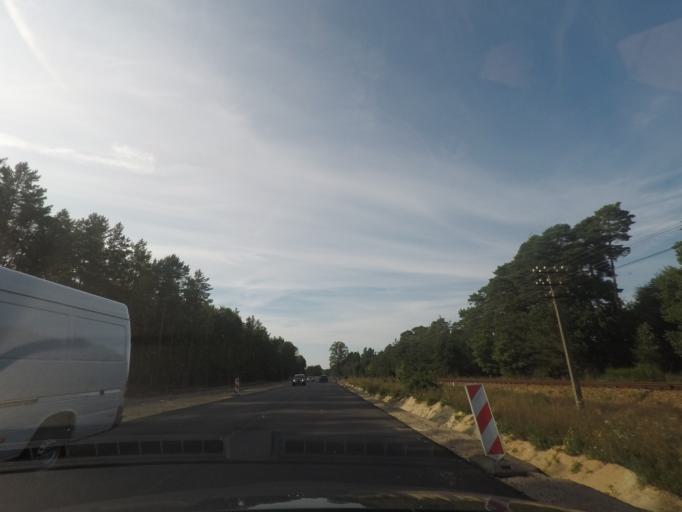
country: PL
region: Pomeranian Voivodeship
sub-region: Powiat leborski
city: Leba
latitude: 54.7210
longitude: 17.5728
